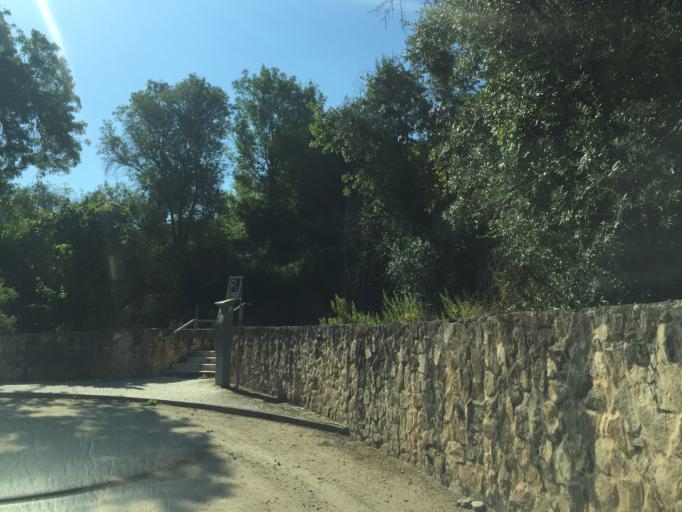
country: PT
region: Santarem
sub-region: Tomar
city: Tomar
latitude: 39.6047
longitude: -8.4176
